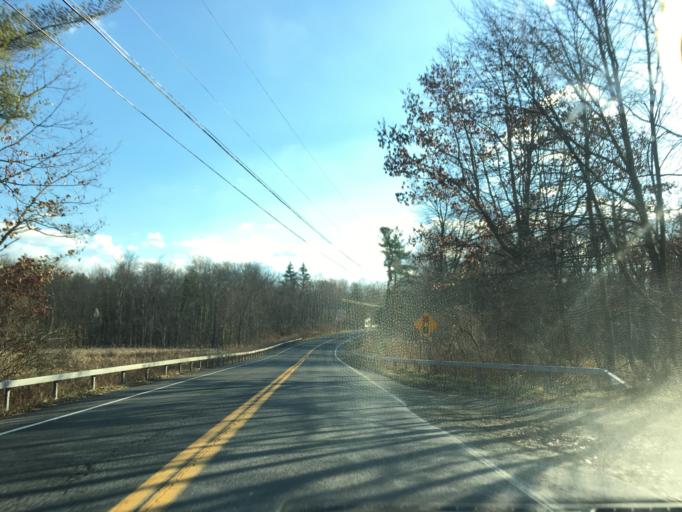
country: US
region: New York
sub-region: Rensselaer County
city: West Sand Lake
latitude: 42.6062
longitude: -73.6096
